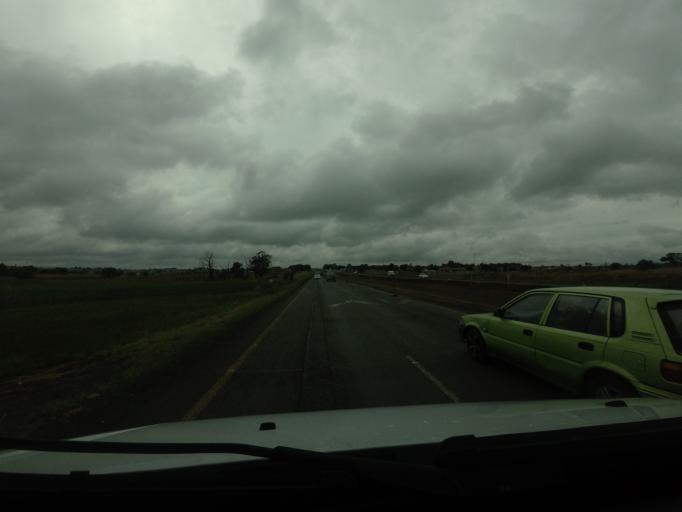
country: ZA
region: Mpumalanga
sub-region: Nkangala District Municipality
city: Witbank
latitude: -25.8812
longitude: 29.1756
